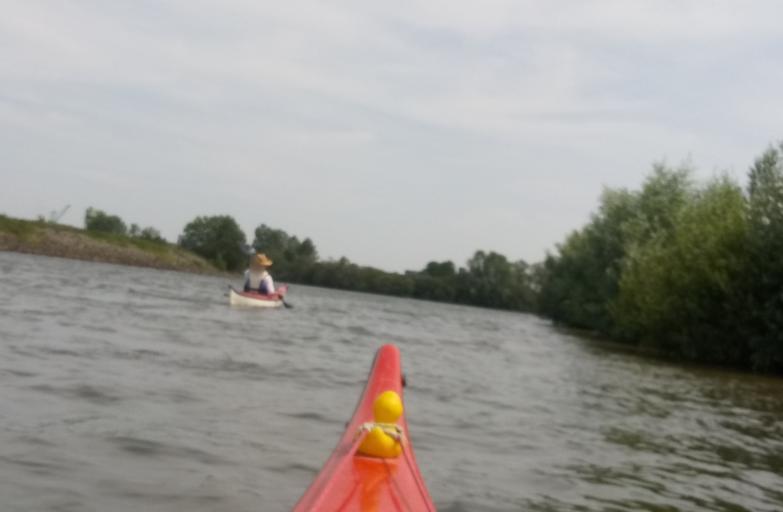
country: NL
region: Gelderland
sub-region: Gemeente Zutphen
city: Zutphen
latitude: 52.1585
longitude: 6.1850
